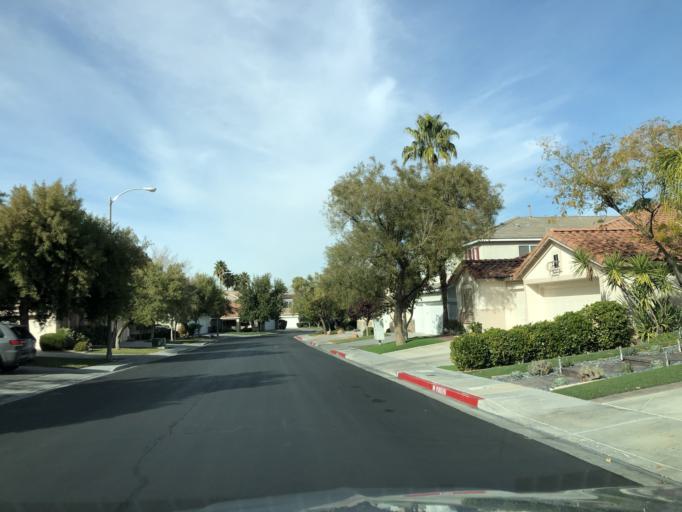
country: US
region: Nevada
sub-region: Clark County
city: Whitney
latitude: 36.0149
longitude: -115.0874
